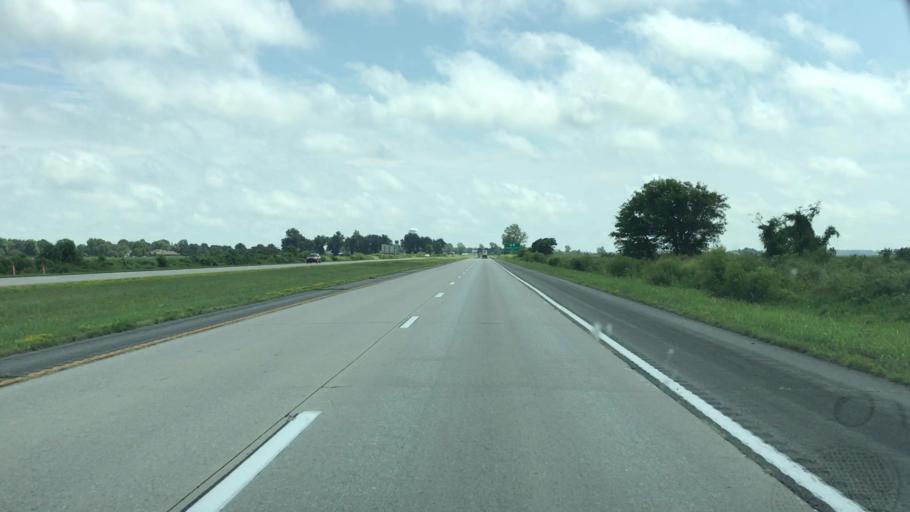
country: US
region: Missouri
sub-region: Pemiscot County
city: Caruthersville
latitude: 36.1650
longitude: -89.6824
